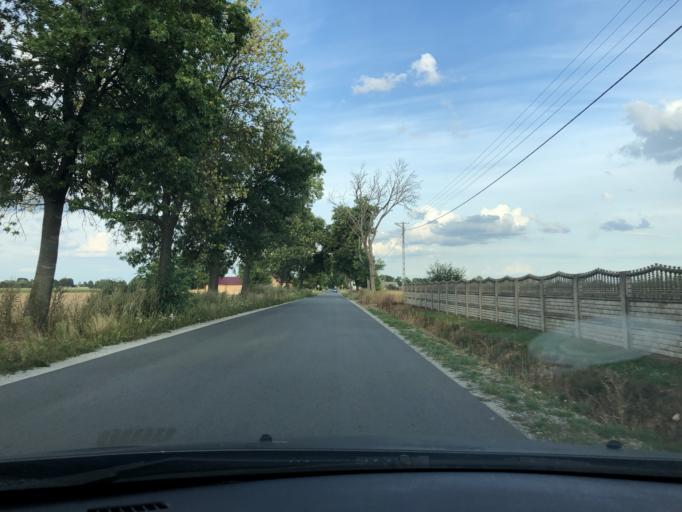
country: PL
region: Lodz Voivodeship
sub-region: Powiat wieruszowski
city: Czastary
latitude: 51.2415
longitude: 18.3545
